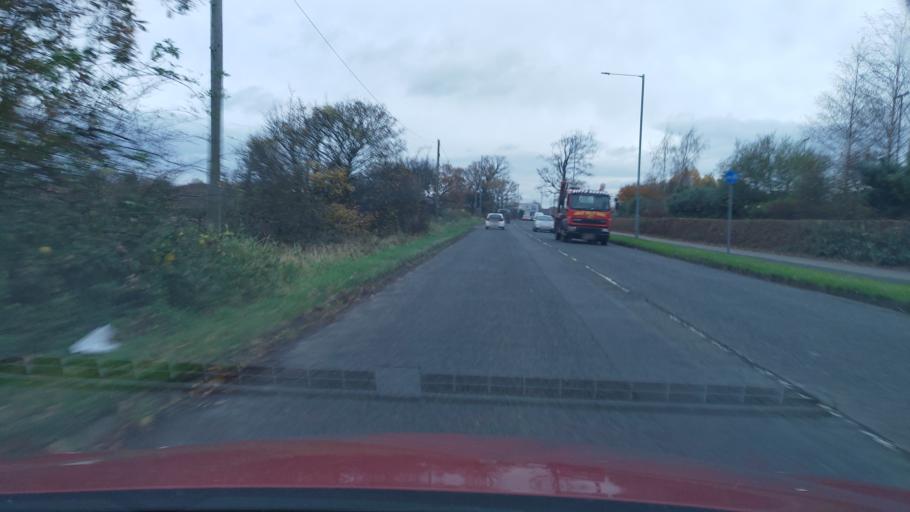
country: GB
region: England
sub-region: Lancashire
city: Euxton
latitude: 53.6844
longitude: -2.6764
